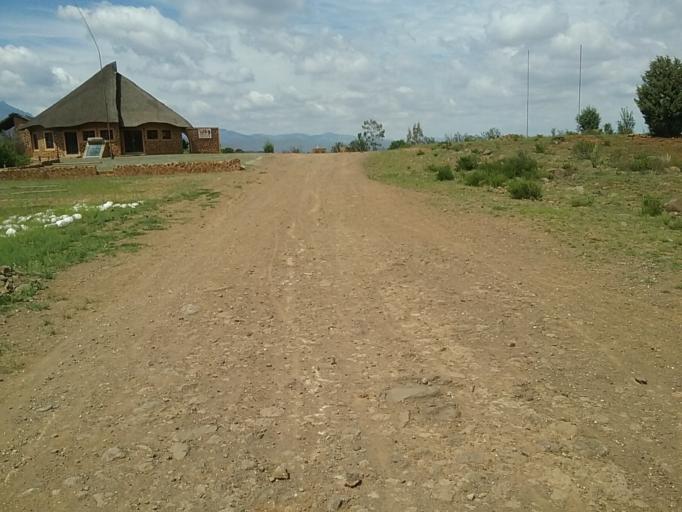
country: LS
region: Berea
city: Teyateyaneng
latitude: -29.2437
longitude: 27.8668
